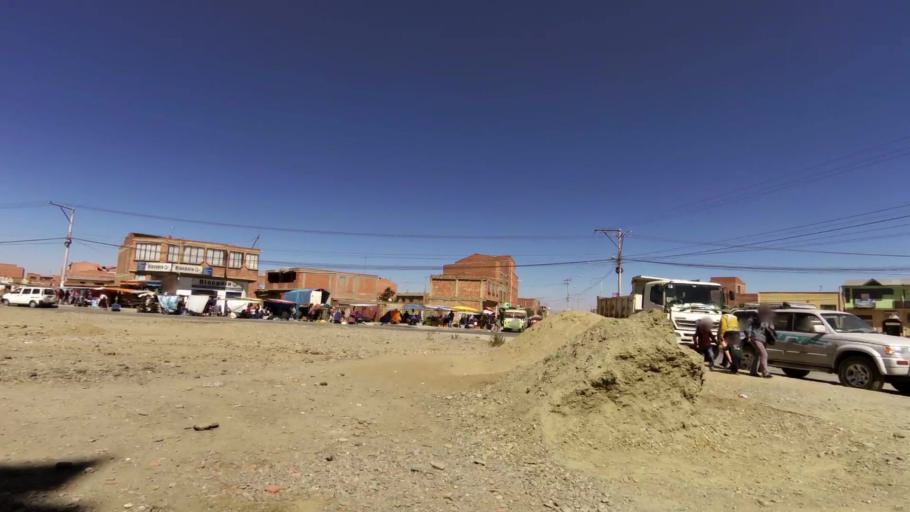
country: BO
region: La Paz
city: La Paz
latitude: -16.5257
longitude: -68.2173
